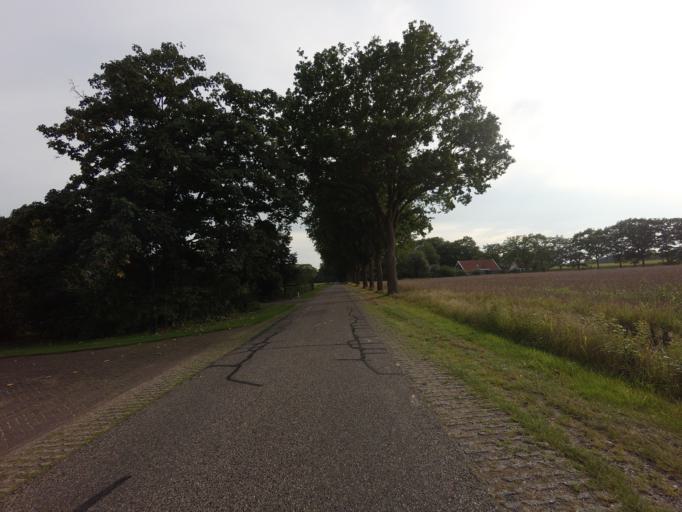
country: NL
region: Overijssel
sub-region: Gemeente Hardenberg
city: Hardenberg
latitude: 52.5930
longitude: 6.6742
